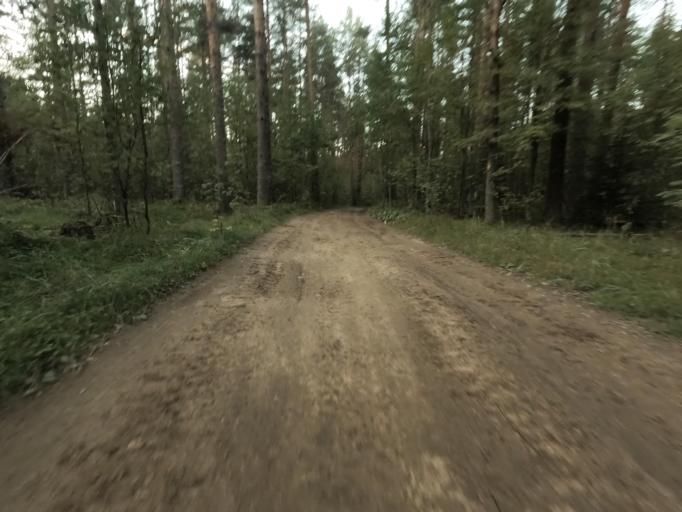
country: RU
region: Leningrad
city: Otradnoye
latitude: 59.8498
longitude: 30.7957
